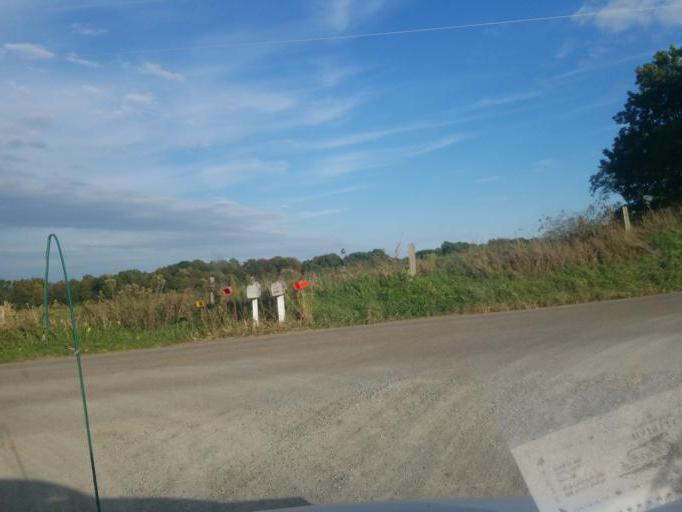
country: US
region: Ohio
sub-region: Wayne County
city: Shreve
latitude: 40.6335
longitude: -82.0815
